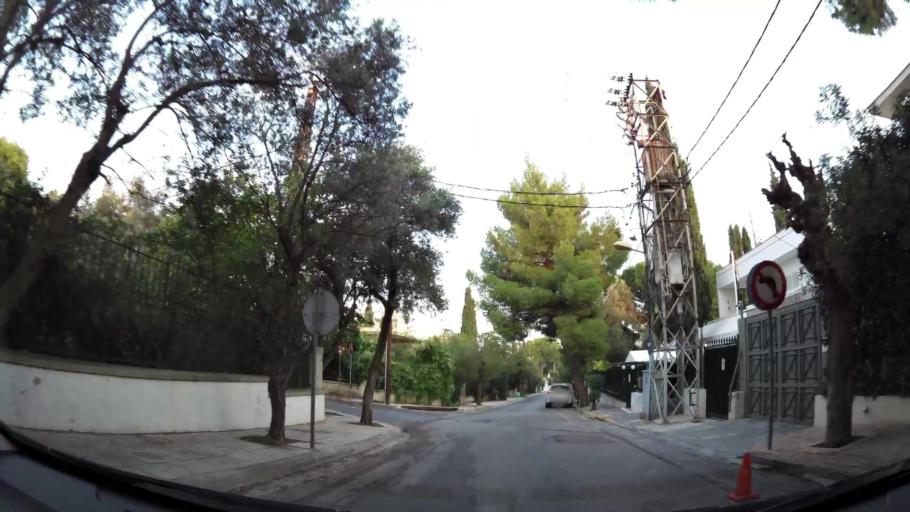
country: GR
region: Attica
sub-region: Nomarchia Athinas
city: Psychiko
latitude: 38.0179
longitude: 23.7734
